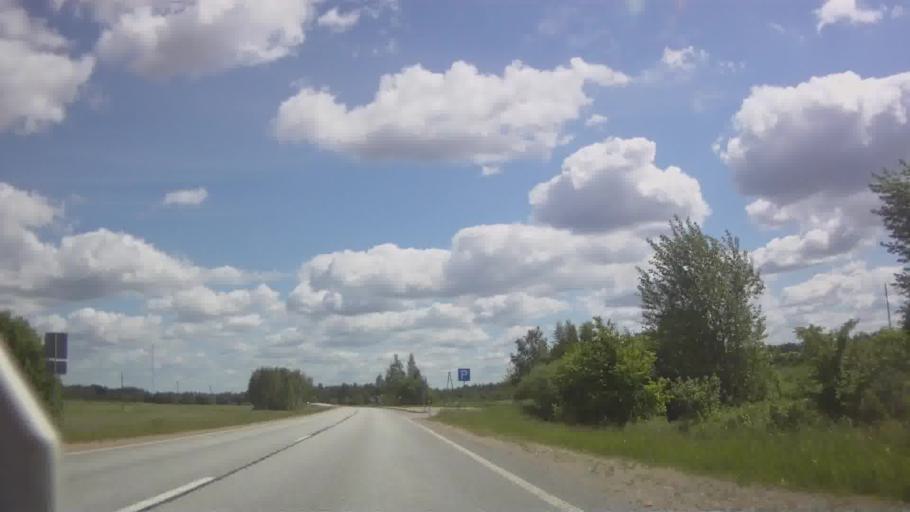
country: LV
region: Varaklani
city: Varaklani
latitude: 56.5213
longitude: 26.4504
